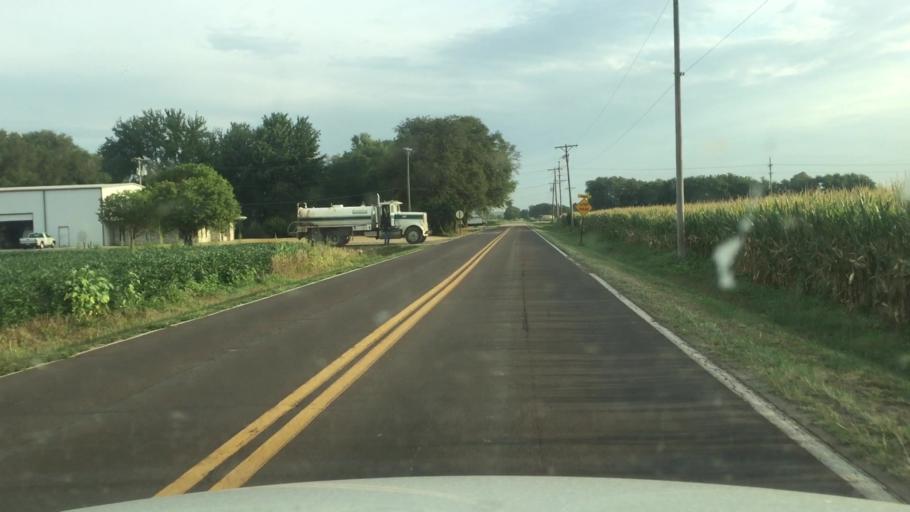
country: US
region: Kansas
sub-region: Shawnee County
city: Topeka
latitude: 39.0568
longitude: -95.6131
